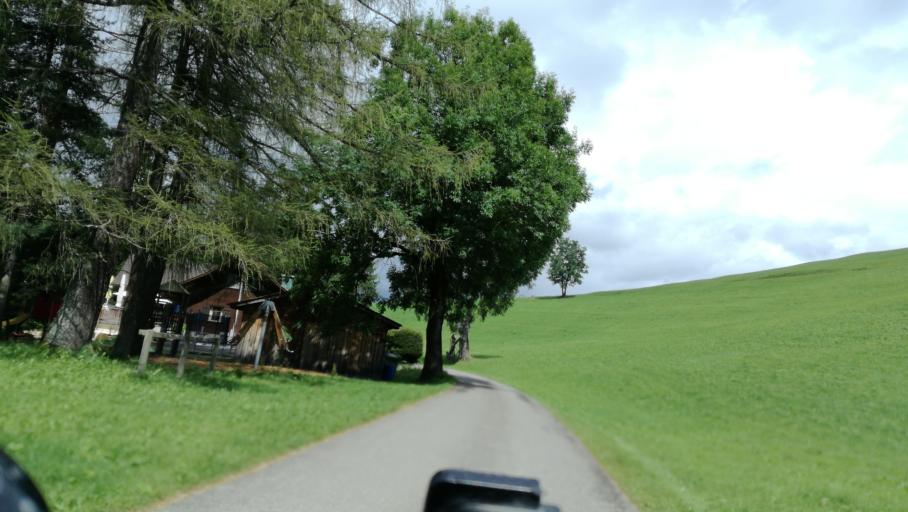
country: CH
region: Zug
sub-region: Zug
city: Walchwil
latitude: 47.1096
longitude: 8.5463
